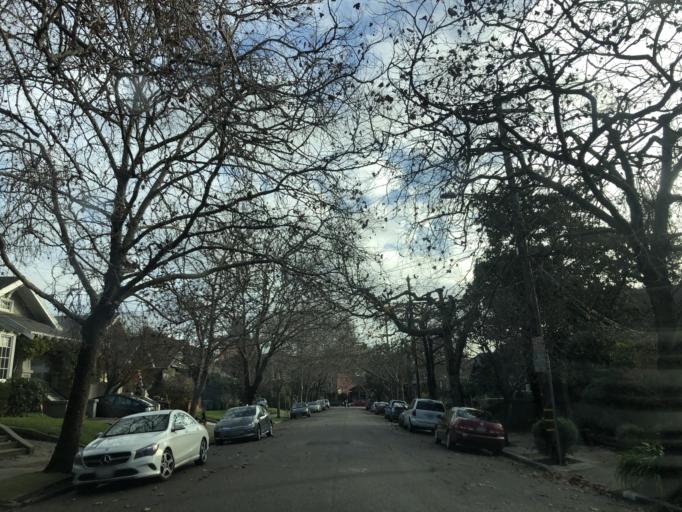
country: US
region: California
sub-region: Alameda County
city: Berkeley
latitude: 37.8523
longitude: -122.2548
